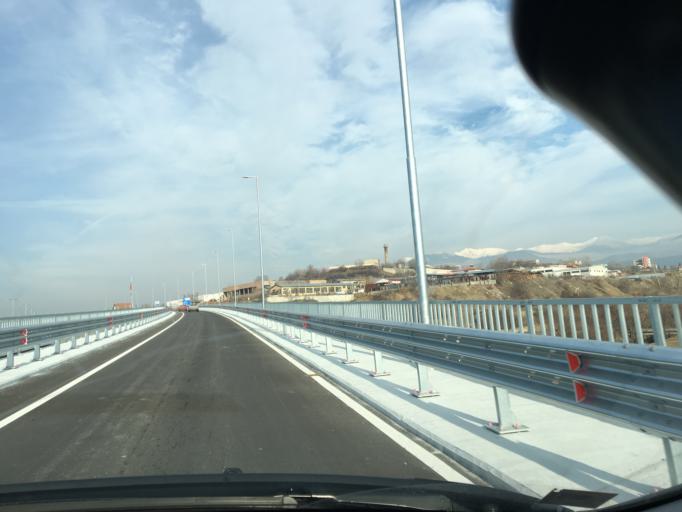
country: BG
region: Blagoevgrad
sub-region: Obshtina Sandanski
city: Sandanski
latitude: 41.5392
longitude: 23.2578
